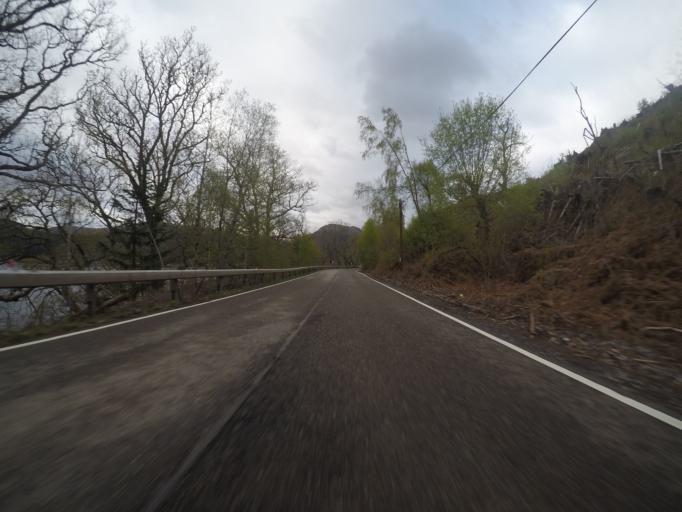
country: GB
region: Scotland
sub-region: Highland
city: Kingussie
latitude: 56.9626
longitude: -4.4544
